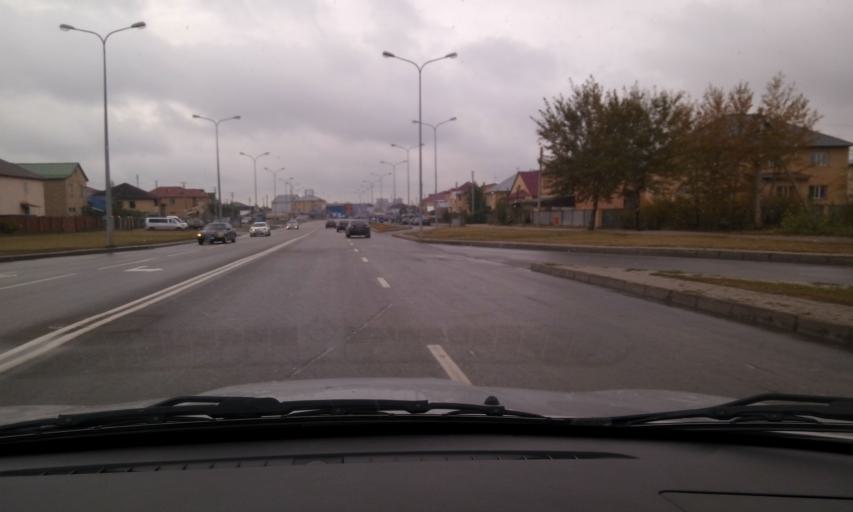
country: KZ
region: Astana Qalasy
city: Astana
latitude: 51.1407
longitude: 71.5216
